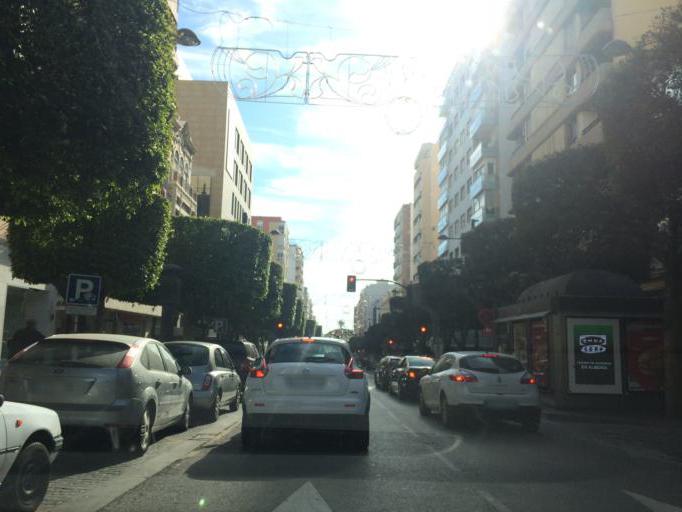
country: ES
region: Andalusia
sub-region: Provincia de Almeria
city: Almeria
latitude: 36.8407
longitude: -2.4638
